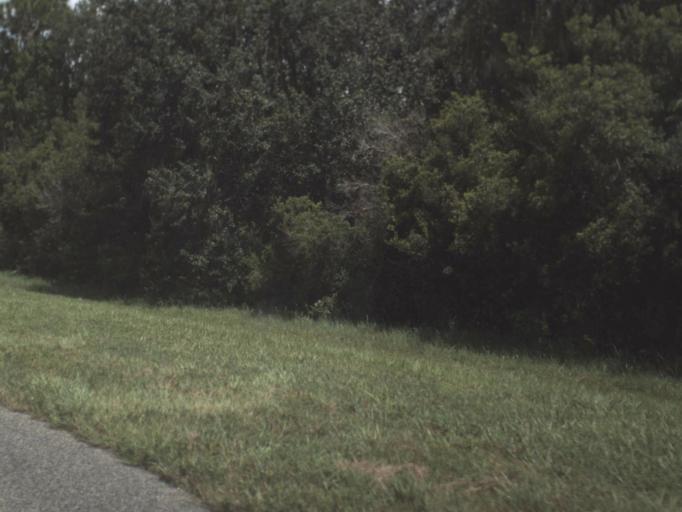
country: US
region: Florida
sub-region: Hardee County
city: Bowling Green
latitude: 27.6579
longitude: -81.8229
